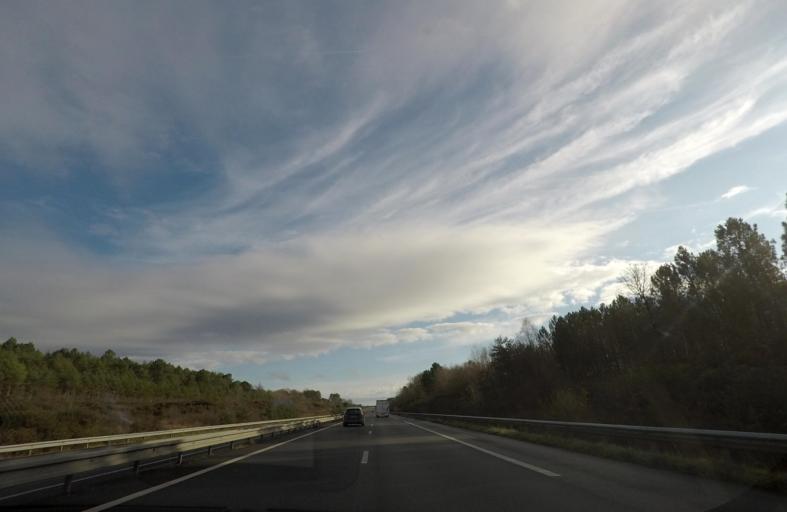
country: FR
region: Centre
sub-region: Departement du Loir-et-Cher
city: Villefranche-sur-Cher
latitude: 47.3146
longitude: 1.8129
